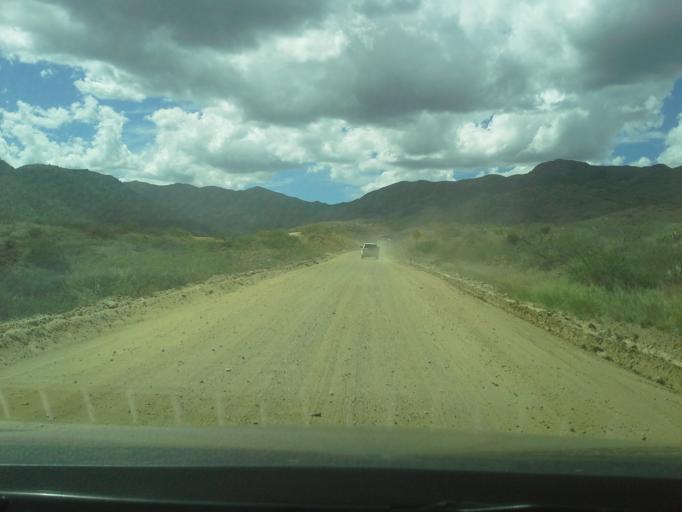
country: US
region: Arizona
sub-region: Yavapai County
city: Spring Valley
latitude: 34.2771
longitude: -112.2518
